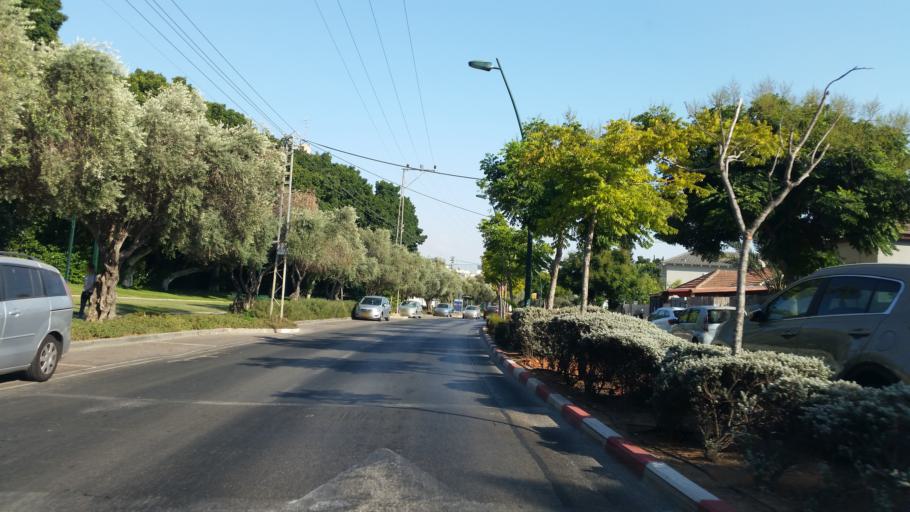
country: IL
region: Tel Aviv
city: Ramat HaSharon
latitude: 32.1302
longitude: 34.8548
